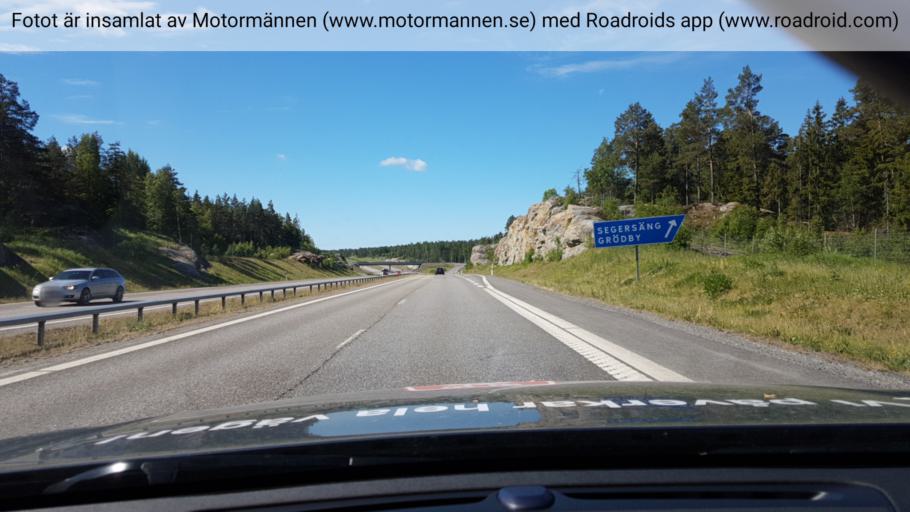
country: SE
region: Stockholm
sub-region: Nynashamns Kommun
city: Osmo
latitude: 59.0313
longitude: 17.9557
